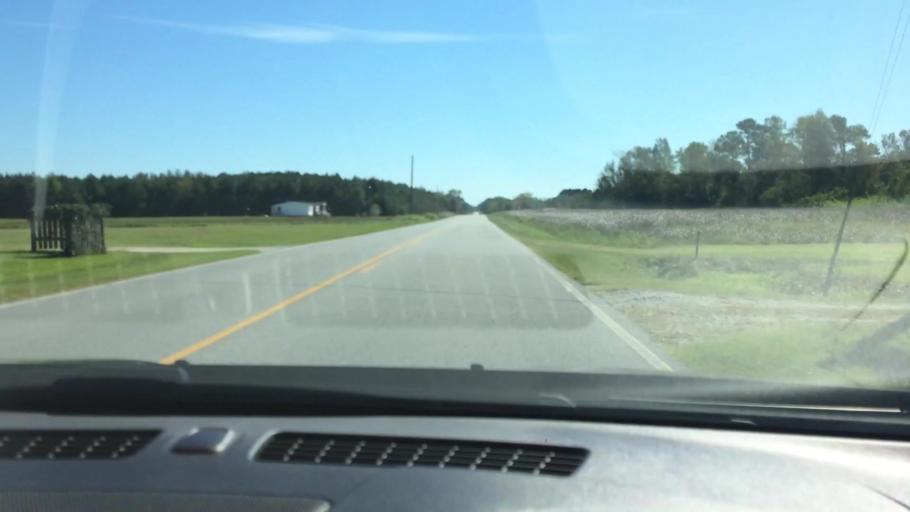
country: US
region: North Carolina
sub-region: Pitt County
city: Grifton
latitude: 35.3953
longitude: -77.3957
